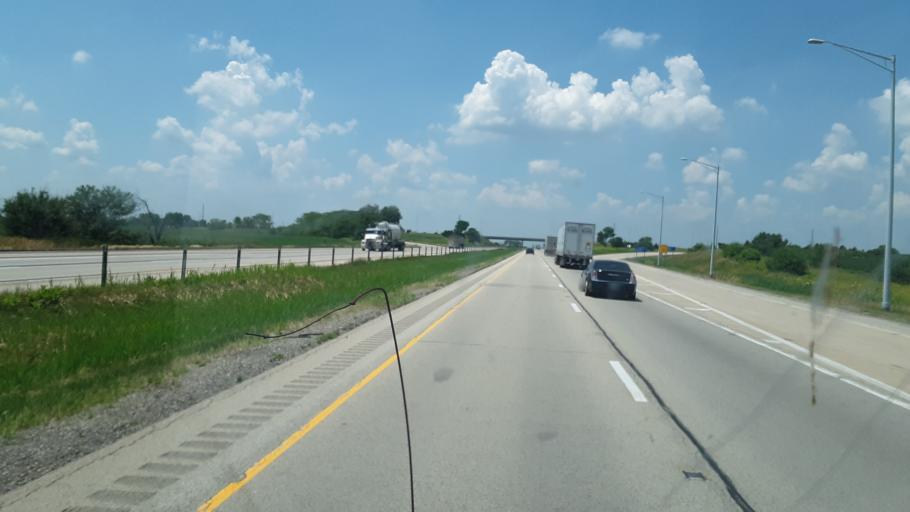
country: US
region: Illinois
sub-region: LaSalle County
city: Marseilles
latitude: 41.3755
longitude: -88.6994
